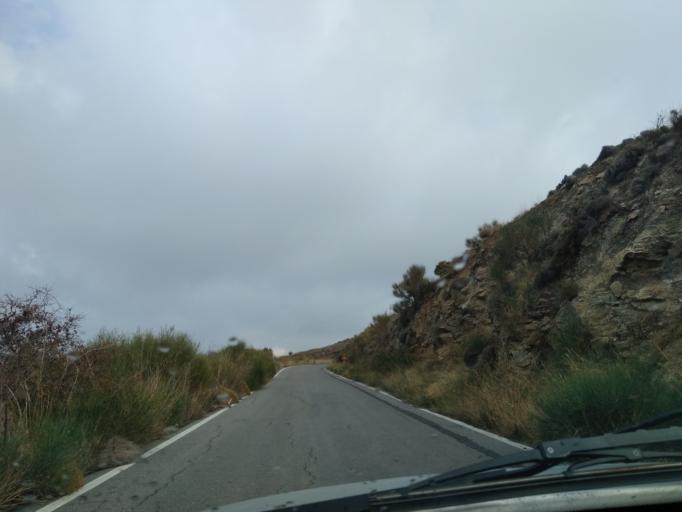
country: GR
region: Crete
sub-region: Nomos Lasithiou
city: Siteia
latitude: 35.1542
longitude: 26.0165
